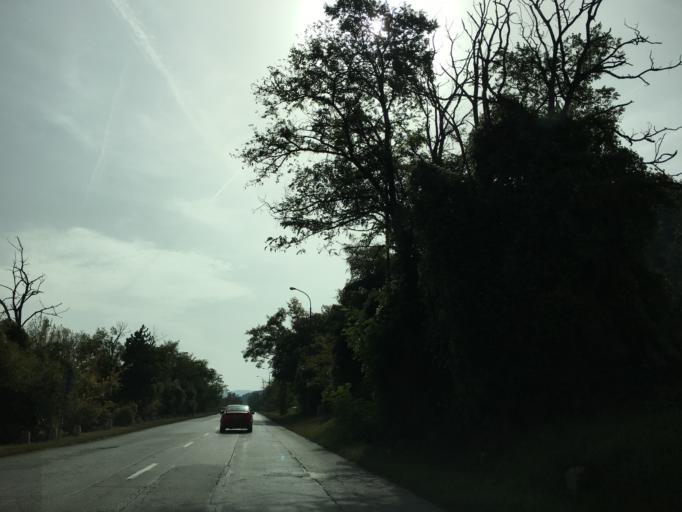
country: BG
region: Sofia-Capital
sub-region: Stolichna Obshtina
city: Sofia
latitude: 42.6070
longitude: 23.4006
